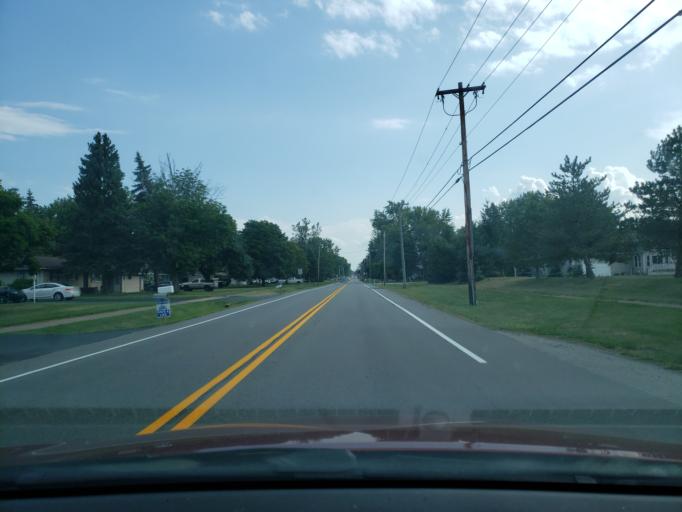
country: US
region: New York
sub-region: Monroe County
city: Greece
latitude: 43.2763
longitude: -77.7149
